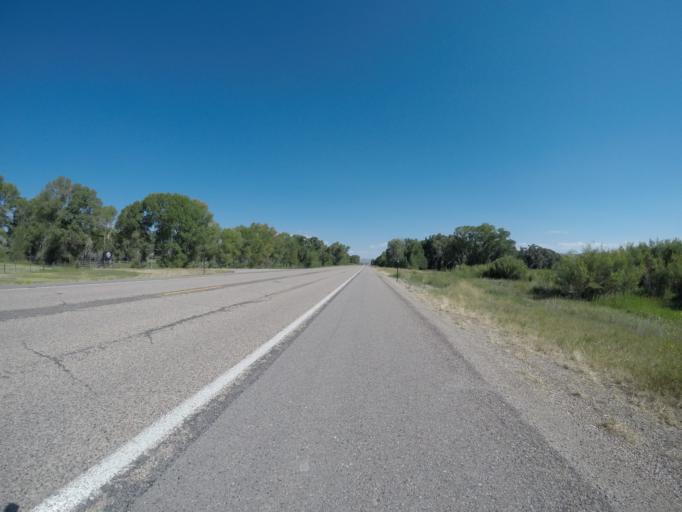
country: US
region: Wyoming
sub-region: Sublette County
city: Marbleton
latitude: 42.2198
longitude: -110.1905
